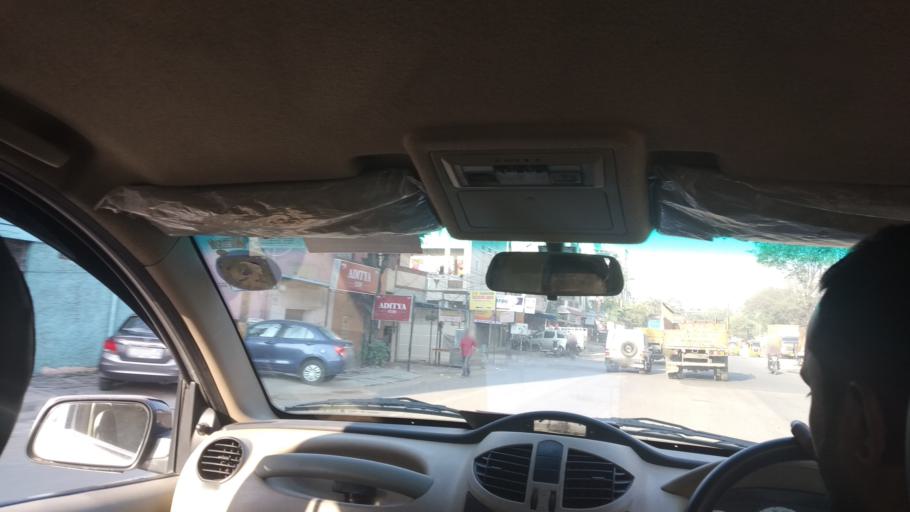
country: IN
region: Telangana
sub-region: Rangareddi
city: Kukatpalli
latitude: 17.4561
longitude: 78.4456
